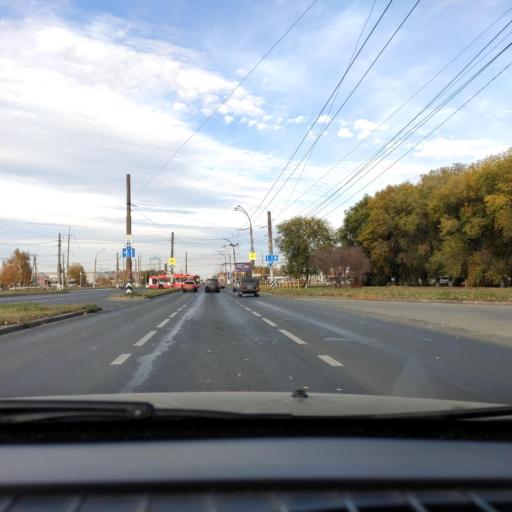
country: RU
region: Samara
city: Tol'yatti
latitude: 53.5383
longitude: 49.2637
